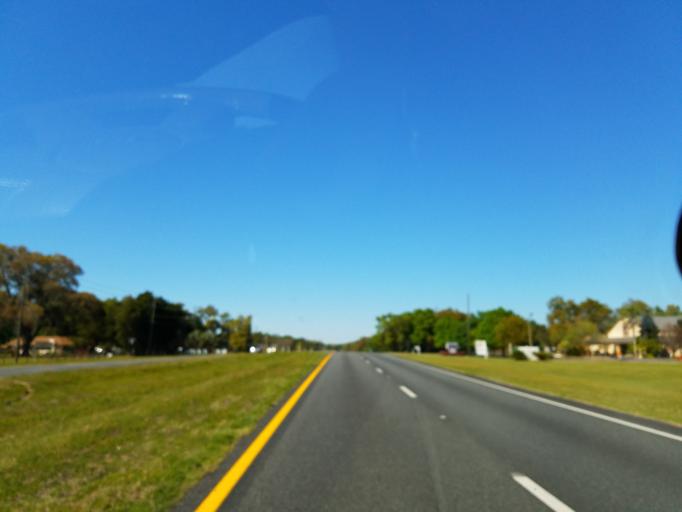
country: US
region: Florida
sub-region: Marion County
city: Belleview
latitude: 29.0421
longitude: -82.0453
